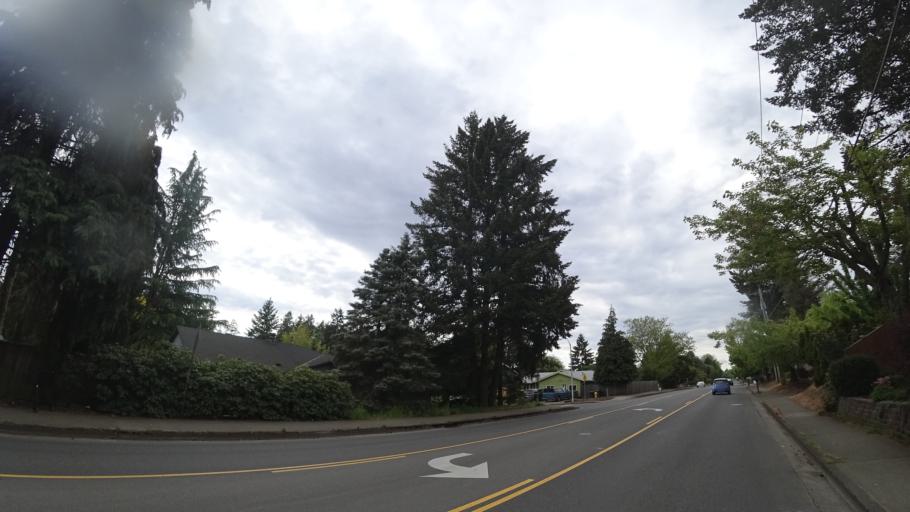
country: US
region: Oregon
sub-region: Washington County
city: Hillsboro
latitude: 45.4987
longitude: -122.9526
